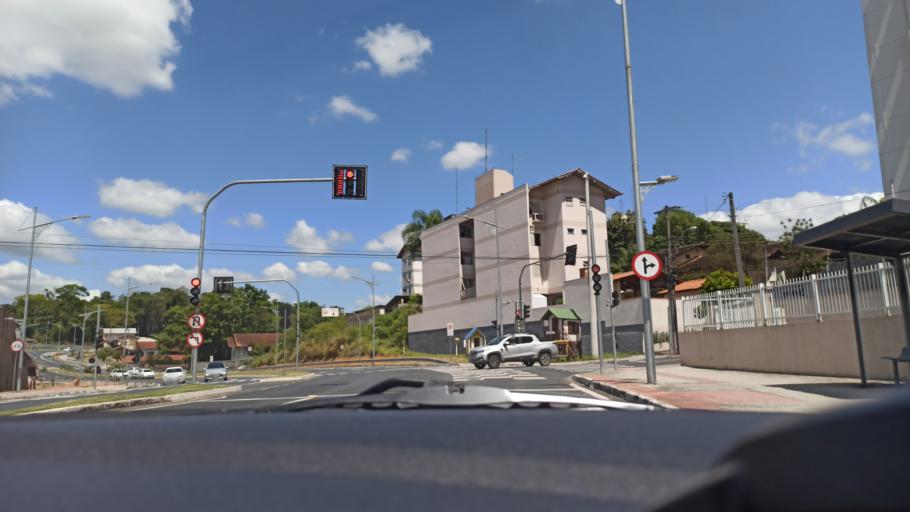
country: BR
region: Santa Catarina
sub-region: Blumenau
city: Blumenau
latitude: -26.9162
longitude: -49.0986
